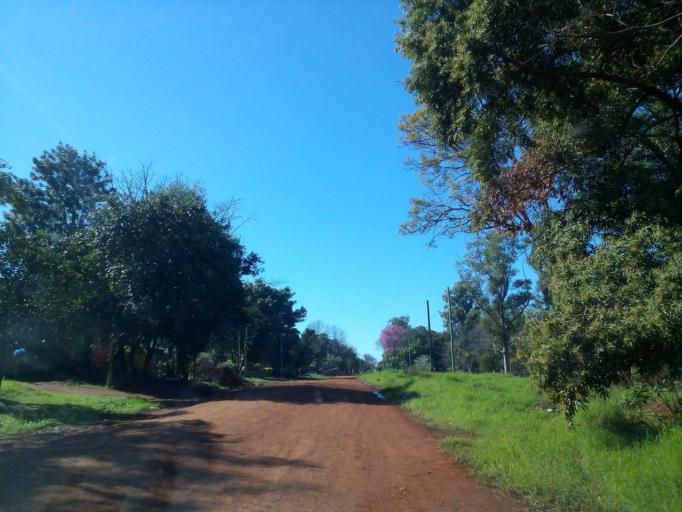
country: AR
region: Misiones
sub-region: Departamento de Capital
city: Posadas
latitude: -27.3906
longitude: -55.9347
